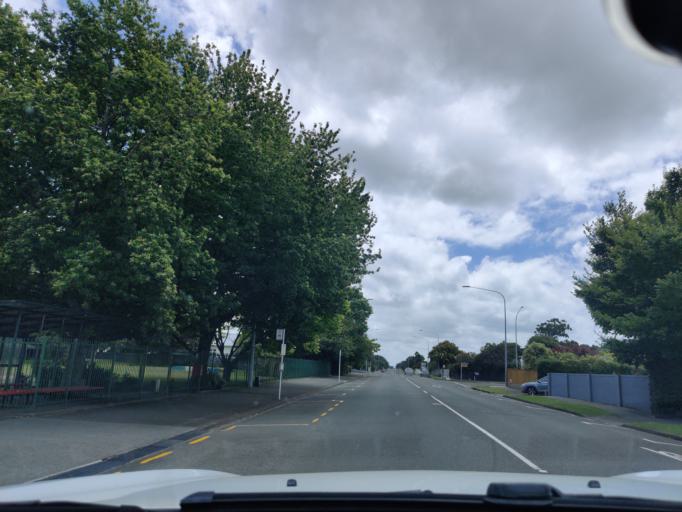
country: NZ
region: Manawatu-Wanganui
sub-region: Palmerston North City
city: Palmerston North
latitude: -40.3610
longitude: 175.6323
